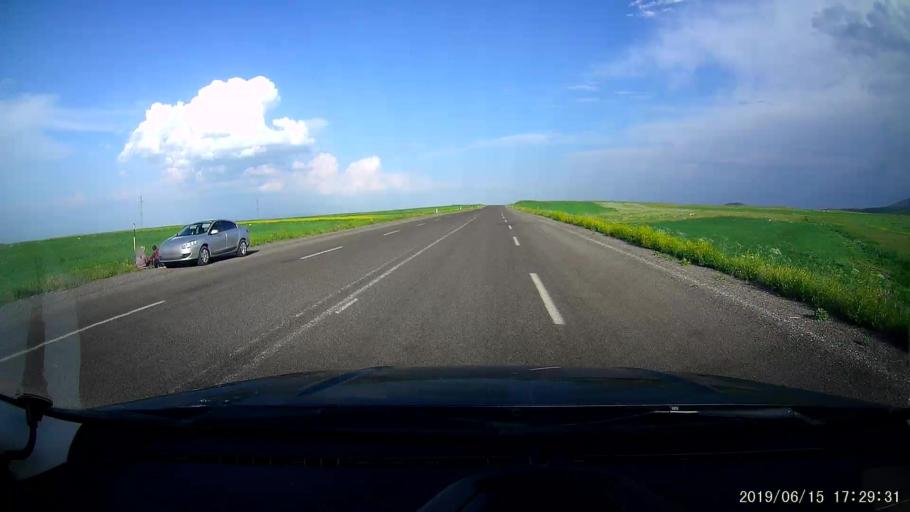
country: TR
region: Kars
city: Basgedikler
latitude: 40.5891
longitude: 43.4534
